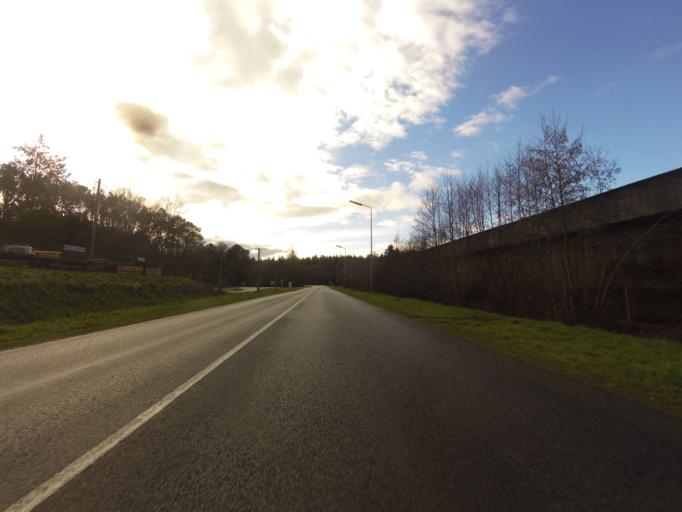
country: FR
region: Brittany
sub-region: Departement du Morbihan
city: Serent
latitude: 47.8181
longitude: -2.5091
